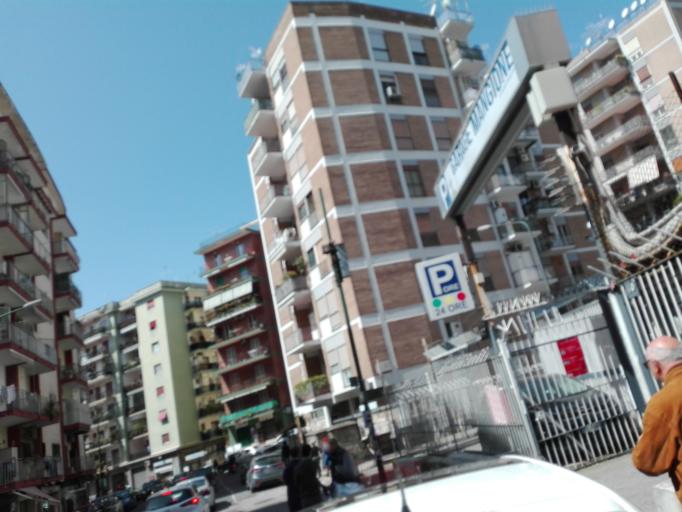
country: IT
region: Campania
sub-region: Provincia di Napoli
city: Napoli
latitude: 40.8517
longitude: 14.2225
